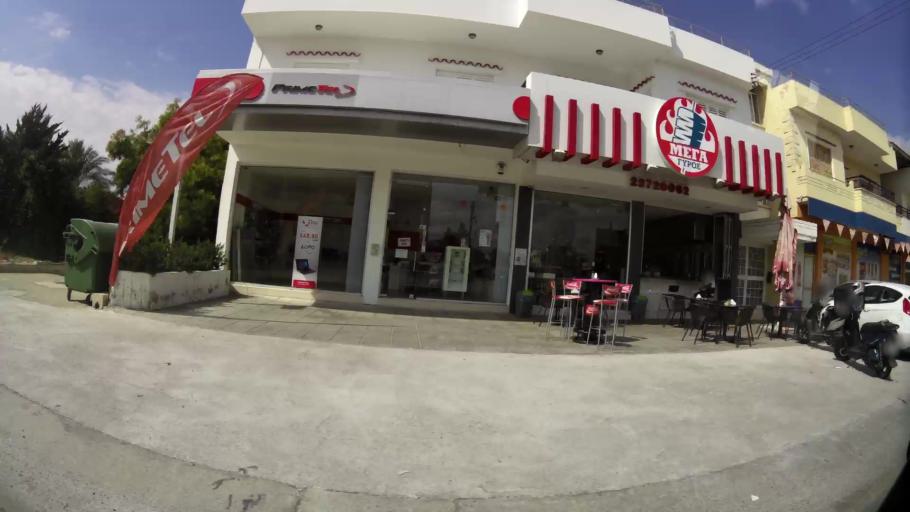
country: CY
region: Lefkosia
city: Tseri
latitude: 35.0823
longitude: 33.3281
